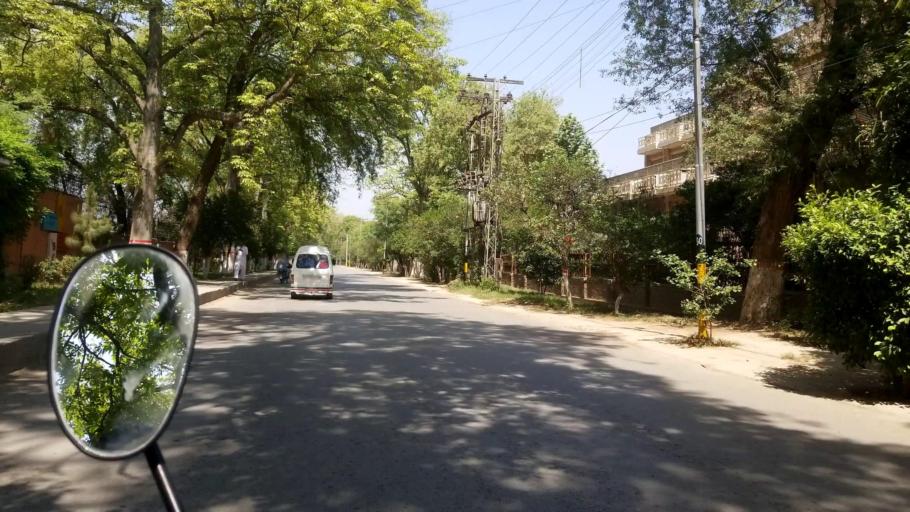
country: PK
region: Khyber Pakhtunkhwa
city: Peshawar
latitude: 34.0080
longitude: 71.4866
